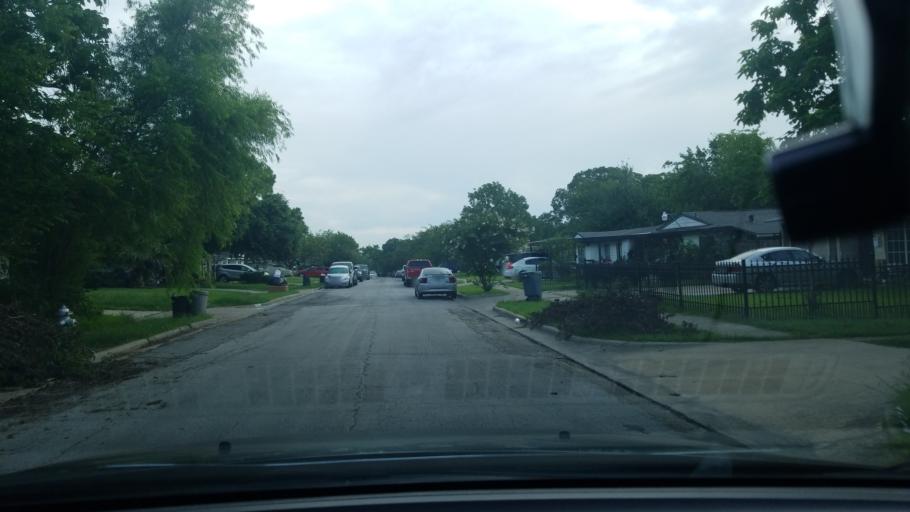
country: US
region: Texas
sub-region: Dallas County
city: Mesquite
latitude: 32.7659
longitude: -96.6381
